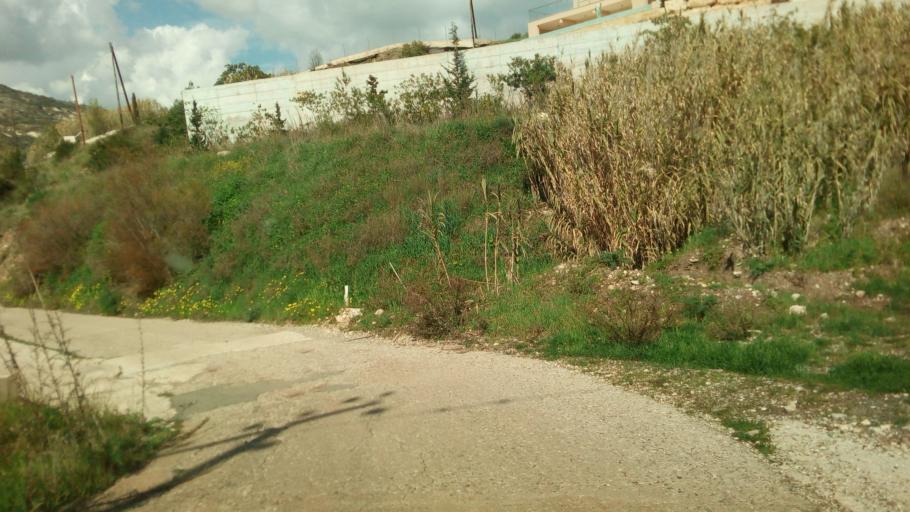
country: CY
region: Pafos
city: Mesogi
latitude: 34.7954
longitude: 32.5327
